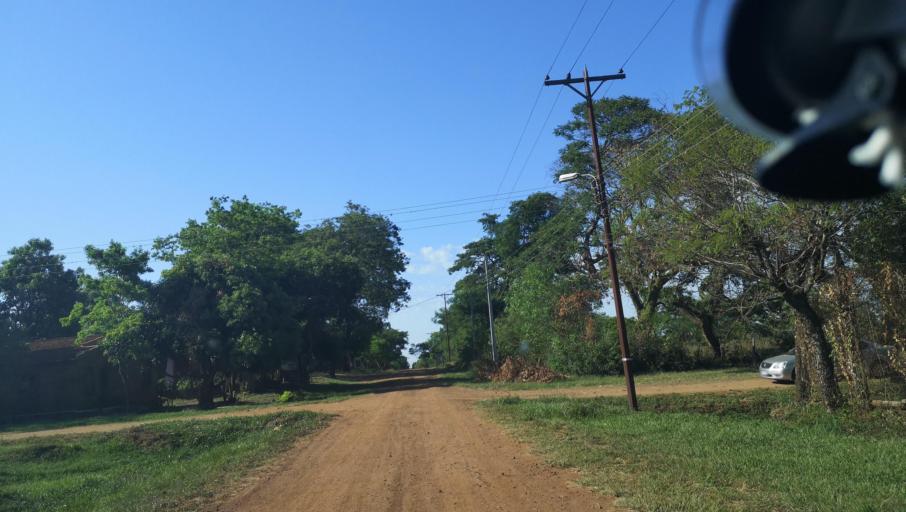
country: PY
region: Itapua
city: Carmen del Parana
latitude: -27.1663
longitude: -56.2385
